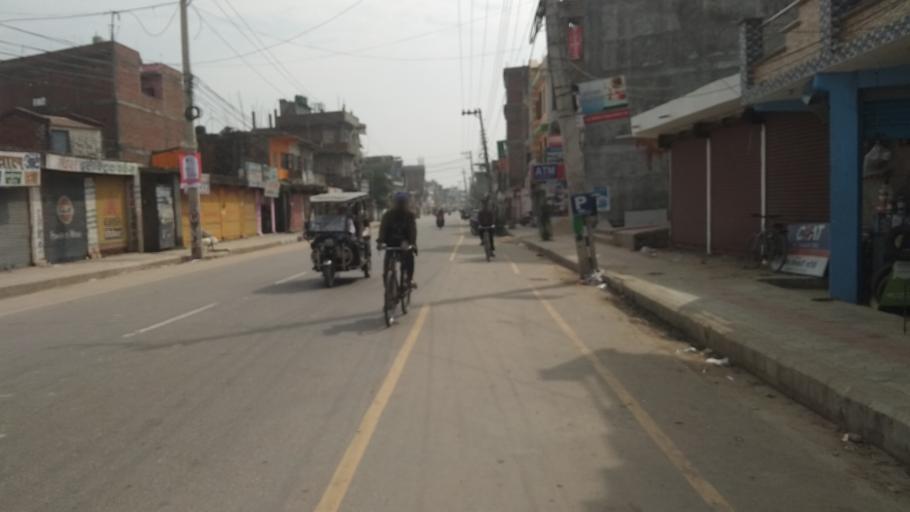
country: NP
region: Central Region
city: Janakpur
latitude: 26.7344
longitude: 85.9324
